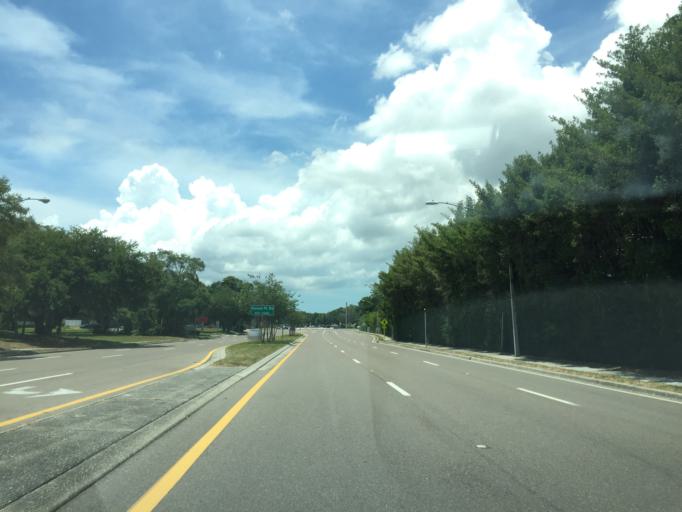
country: US
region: Florida
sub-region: Pinellas County
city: Dunedin
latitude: 27.9920
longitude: -82.7436
